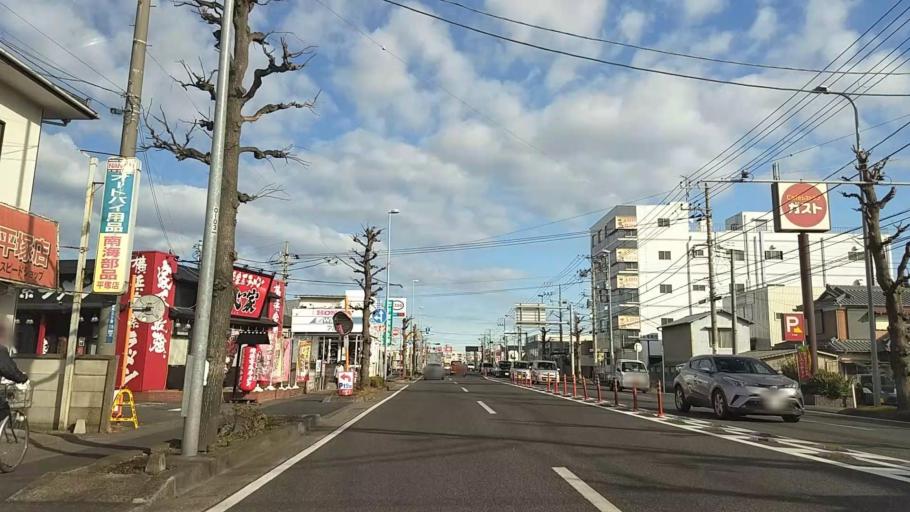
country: JP
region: Kanagawa
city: Hiratsuka
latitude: 35.3565
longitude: 139.3575
